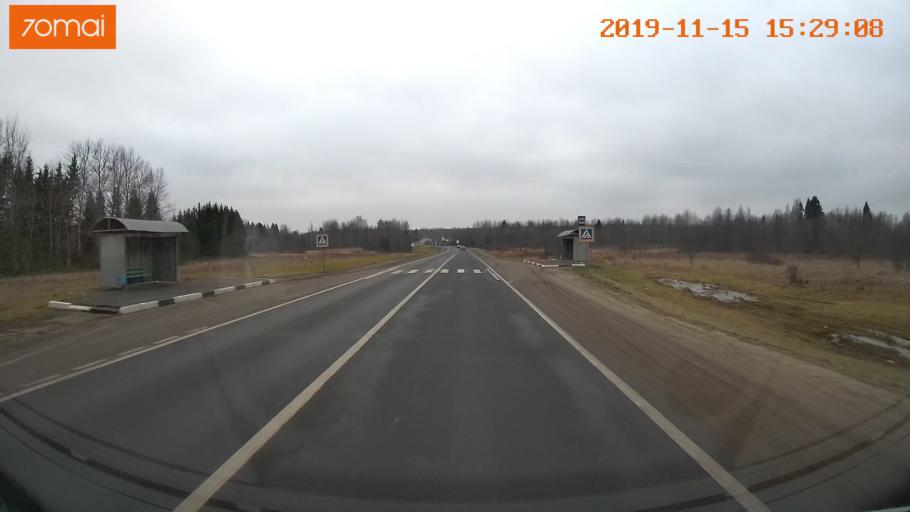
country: RU
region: Jaroslavl
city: Danilov
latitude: 58.1241
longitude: 40.1242
